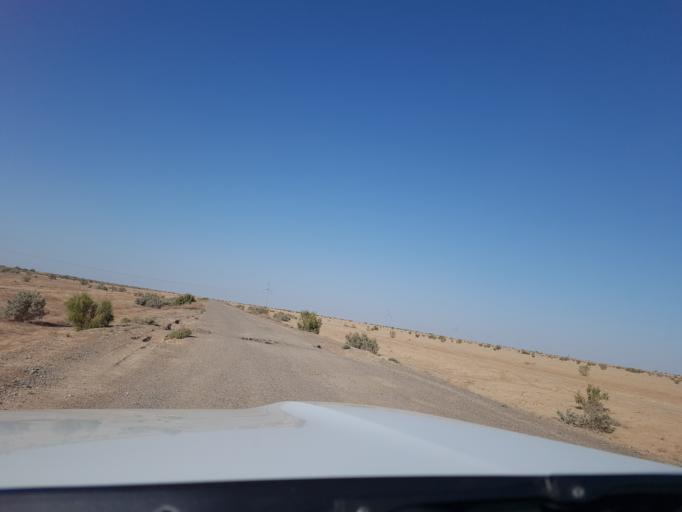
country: IR
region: Razavi Khorasan
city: Sarakhs
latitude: 36.8482
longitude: 61.3366
